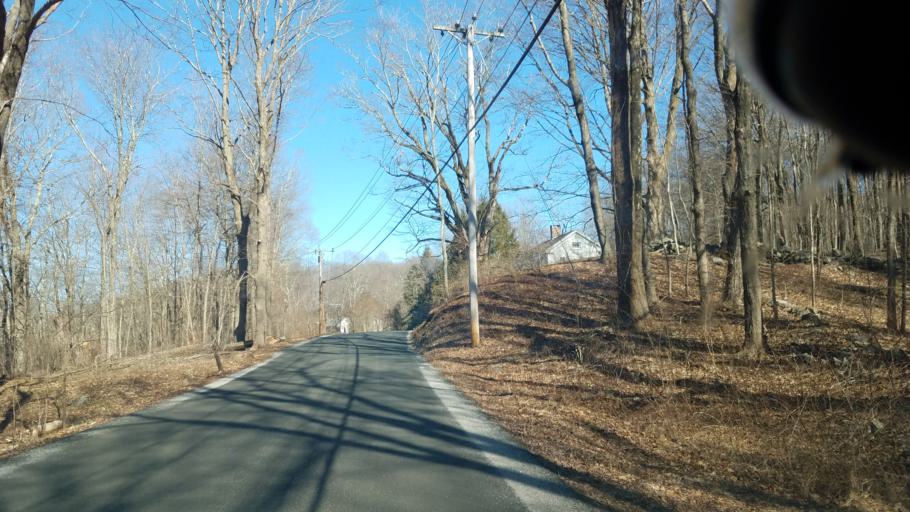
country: US
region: Connecticut
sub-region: Fairfield County
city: Newtown
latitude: 41.3495
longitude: -73.3178
